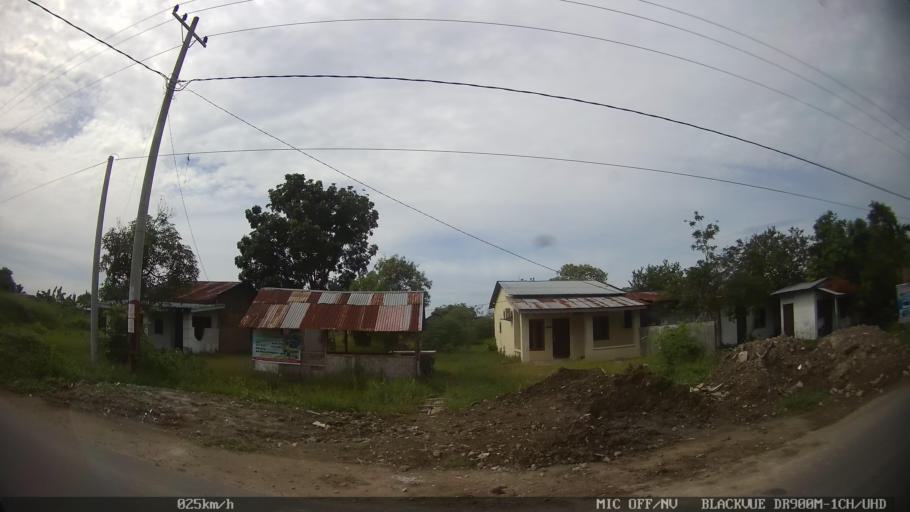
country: ID
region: North Sumatra
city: Medan
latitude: 3.6196
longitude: 98.7580
